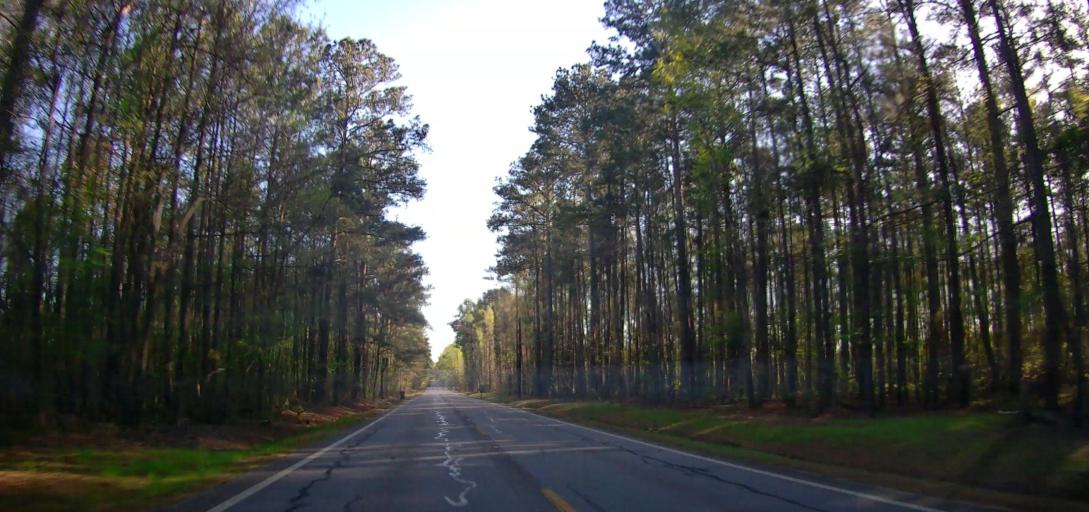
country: US
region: Georgia
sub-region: Butts County
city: Indian Springs
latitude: 33.2244
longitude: -83.9283
